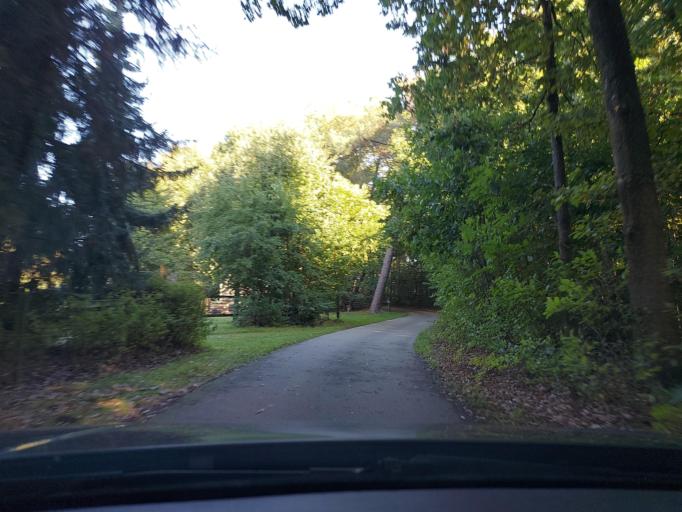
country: BE
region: Flanders
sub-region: Provincie Antwerpen
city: Meerhout
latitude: 51.1103
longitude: 5.0463
